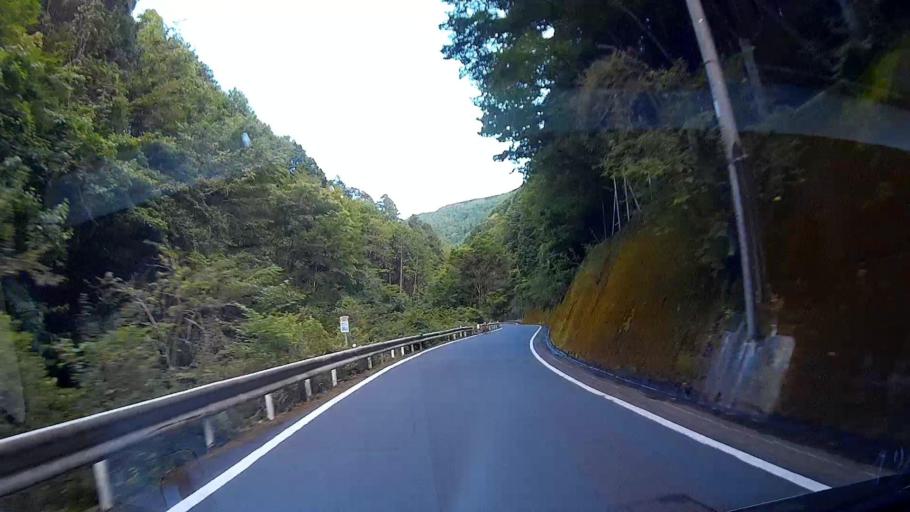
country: JP
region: Shizuoka
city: Shizuoka-shi
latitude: 35.1565
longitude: 138.2553
